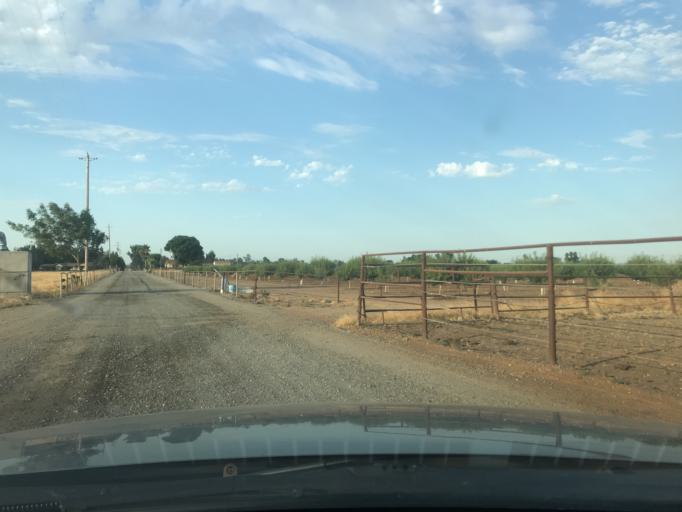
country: US
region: California
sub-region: Merced County
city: Merced
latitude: 37.3721
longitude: -120.4986
